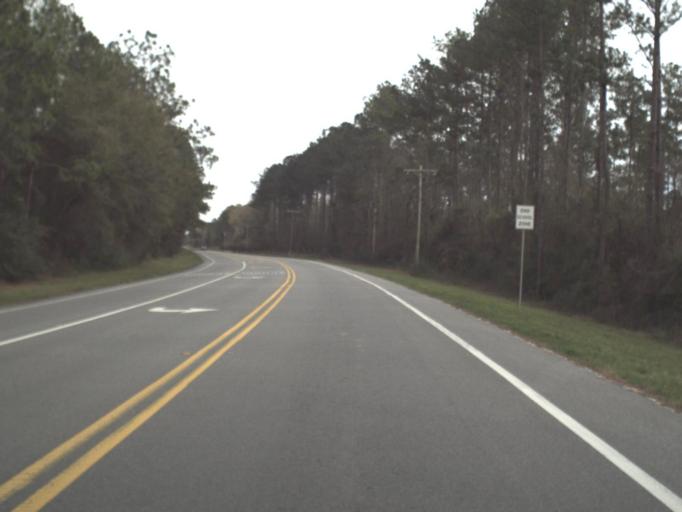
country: US
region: Florida
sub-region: Wakulla County
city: Crawfordville
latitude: 30.2582
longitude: -84.3535
